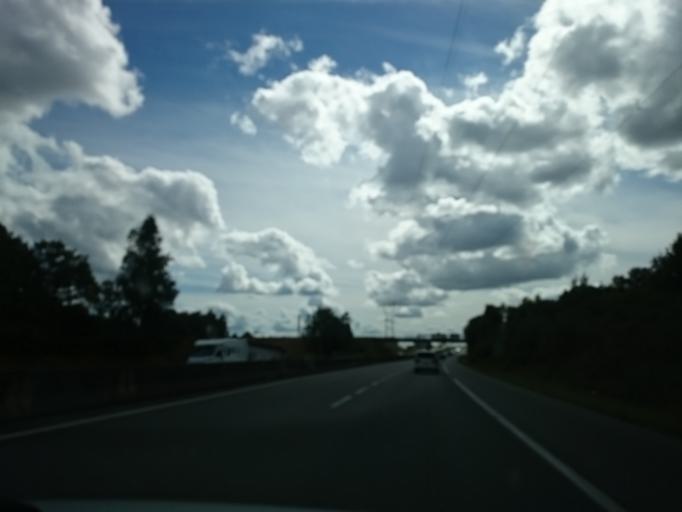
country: FR
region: Pays de la Loire
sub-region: Departement de la Loire-Atlantique
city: Saint-Sebastien-sur-Loire
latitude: 47.1942
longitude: -1.4875
